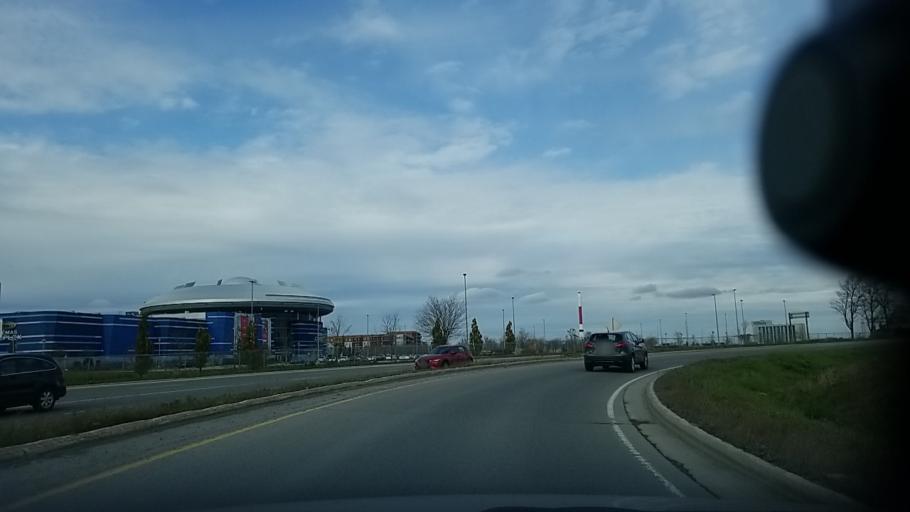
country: CA
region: Quebec
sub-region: Laval
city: Laval
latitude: 45.5625
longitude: -73.7395
